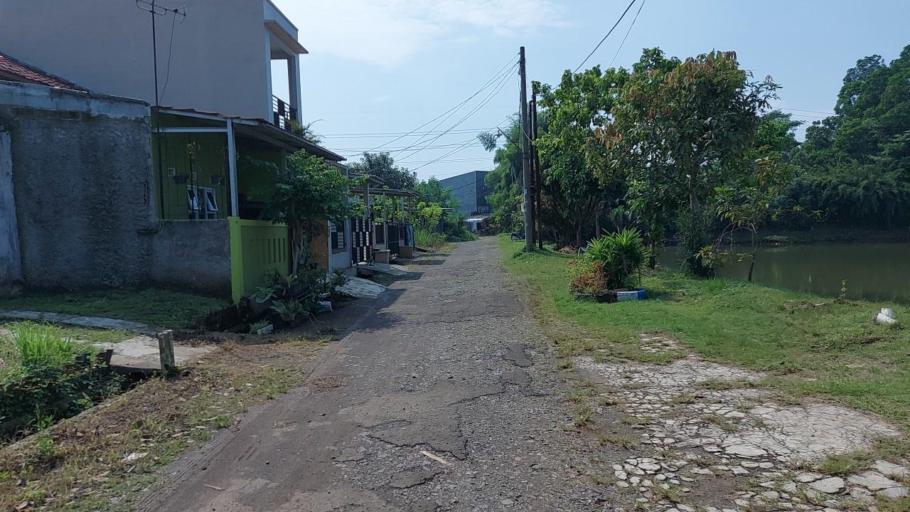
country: ID
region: West Java
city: Cibinong
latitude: -6.5101
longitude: 106.7849
